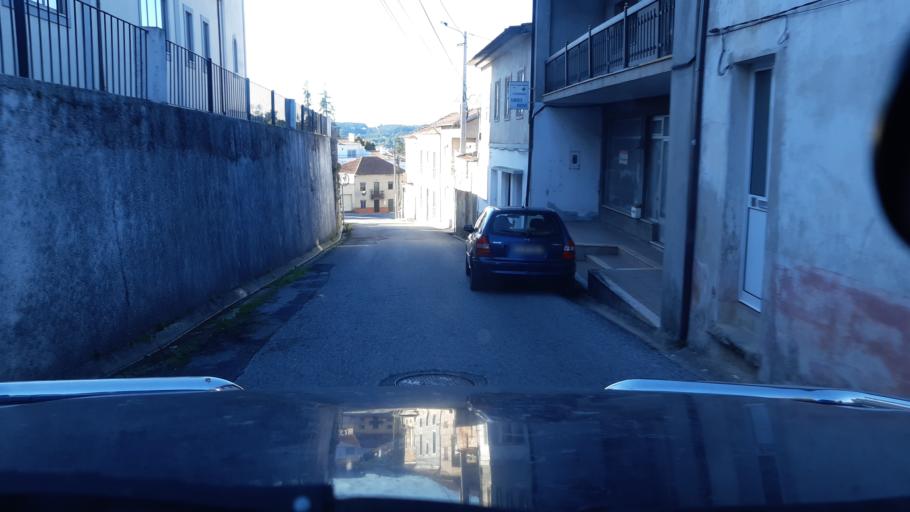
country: PT
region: Aveiro
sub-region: Agueda
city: Agueda
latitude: 40.5586
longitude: -8.4381
